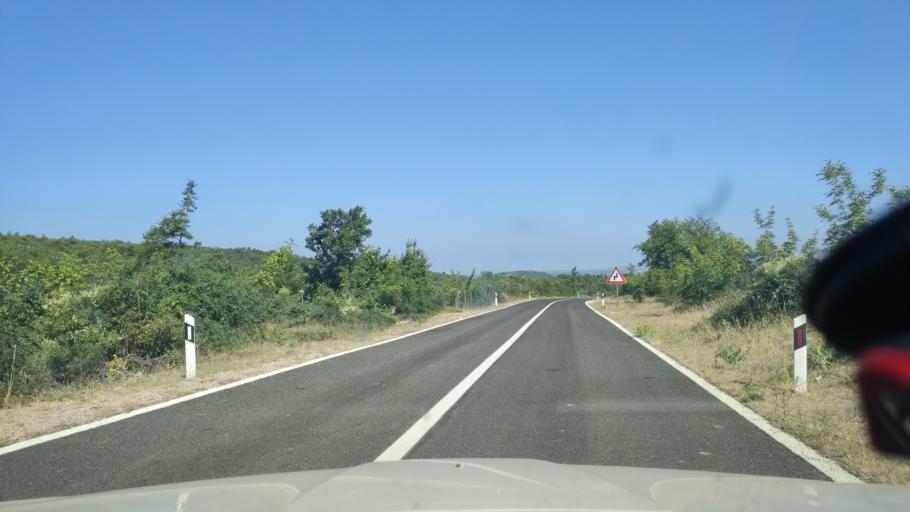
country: HR
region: Sibensko-Kniniska
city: Zaton
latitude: 43.9117
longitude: 15.8386
